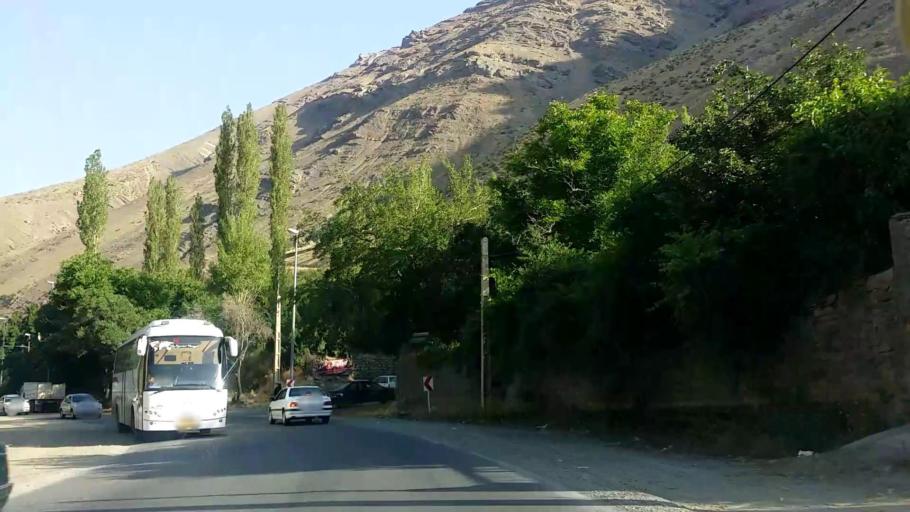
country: IR
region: Alborz
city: Karaj
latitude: 36.0387
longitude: 51.1904
